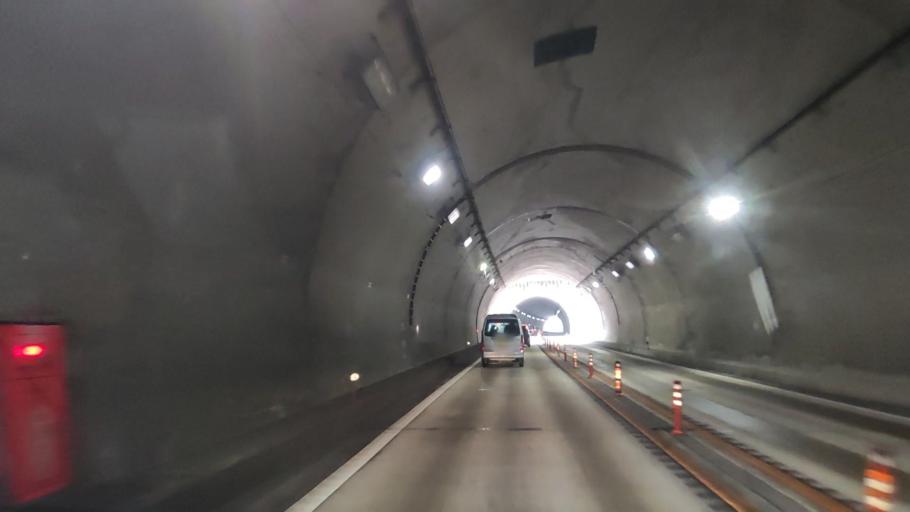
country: JP
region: Tokushima
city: Kamojimacho-jogejima
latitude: 34.1090
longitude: 134.3160
